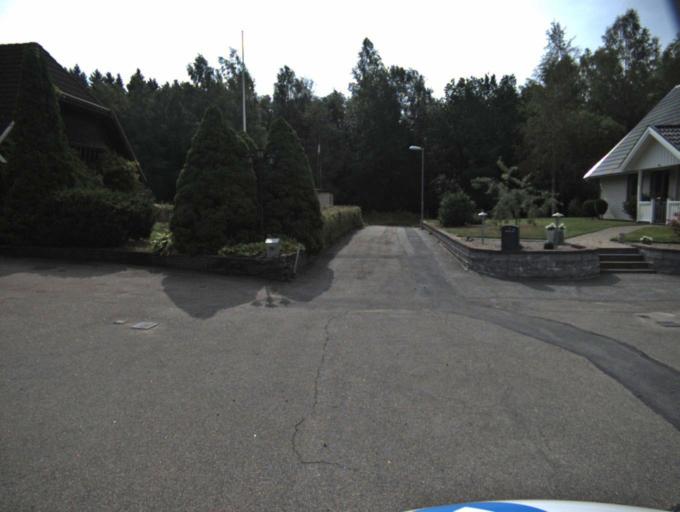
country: SE
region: Vaestra Goetaland
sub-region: Ulricehamns Kommun
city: Ulricehamn
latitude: 57.7770
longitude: 13.4223
